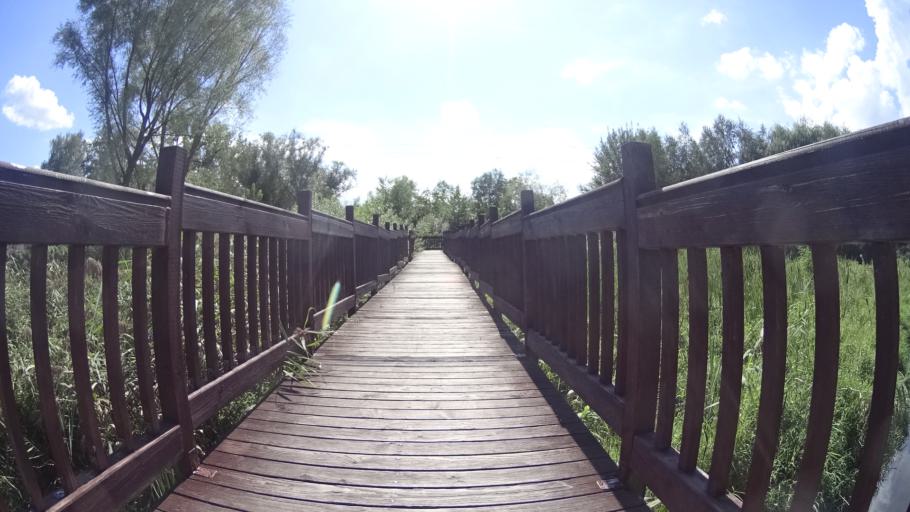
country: PL
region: Masovian Voivodeship
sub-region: Powiat grojecki
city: Mogielnica
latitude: 51.6969
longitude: 20.7230
